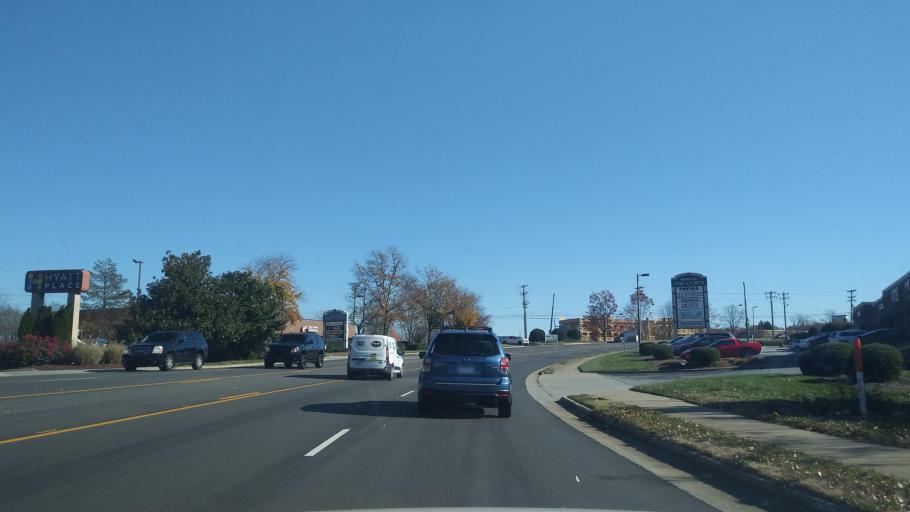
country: US
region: North Carolina
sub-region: Guilford County
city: Jamestown
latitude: 36.0542
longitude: -79.8919
